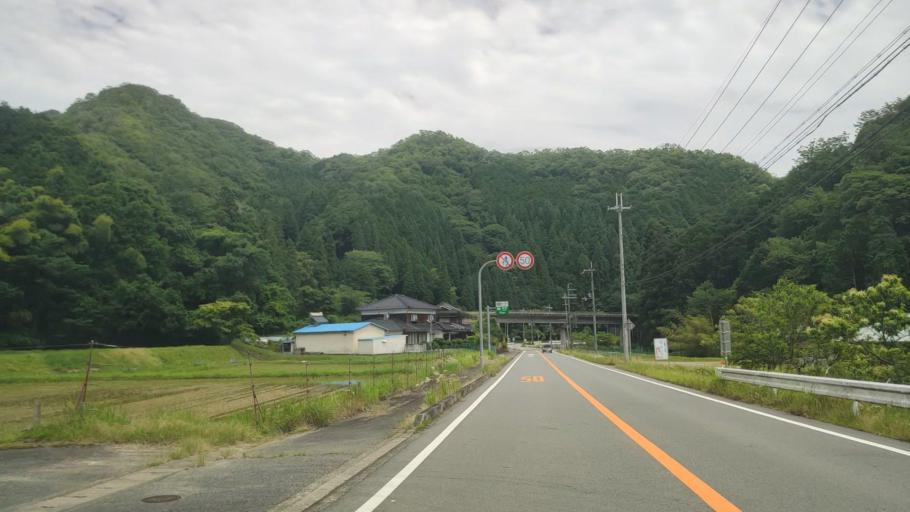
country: JP
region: Hyogo
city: Yamazakicho-nakabirose
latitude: 35.0721
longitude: 134.3579
